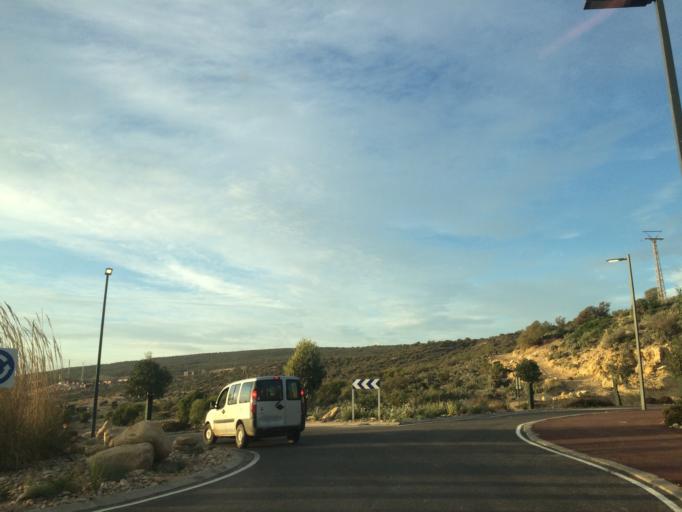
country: MA
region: Souss-Massa-Draa
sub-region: Agadir-Ida-ou-Tnan
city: Taghazout
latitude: 30.5390
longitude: -9.6963
